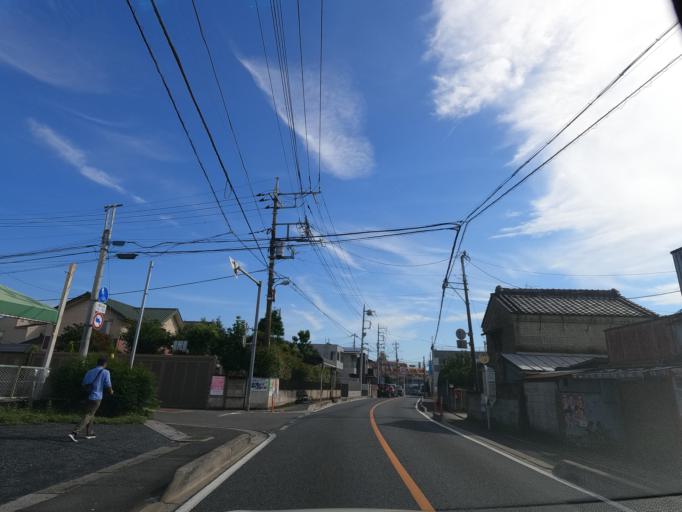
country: JP
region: Saitama
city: Yono
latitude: 35.8830
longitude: 139.6114
